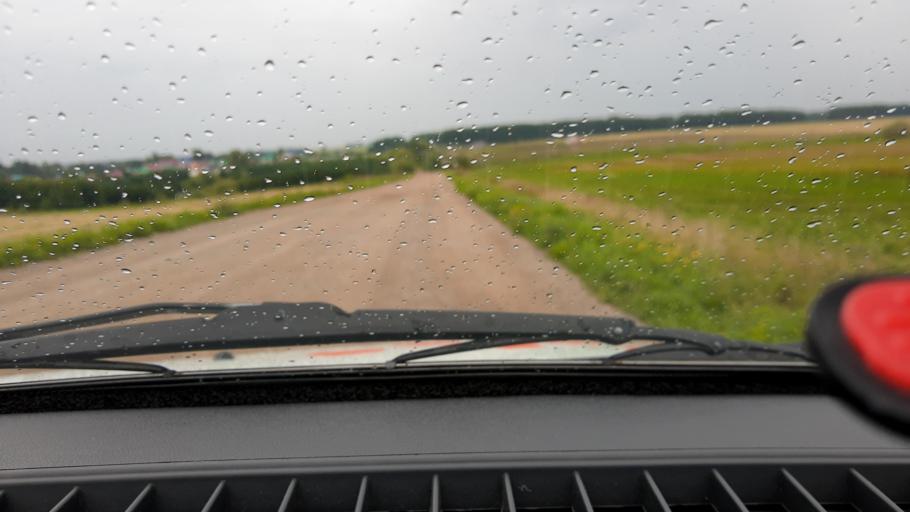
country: RU
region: Bashkortostan
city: Karmaskaly
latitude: 54.3849
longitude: 56.1186
